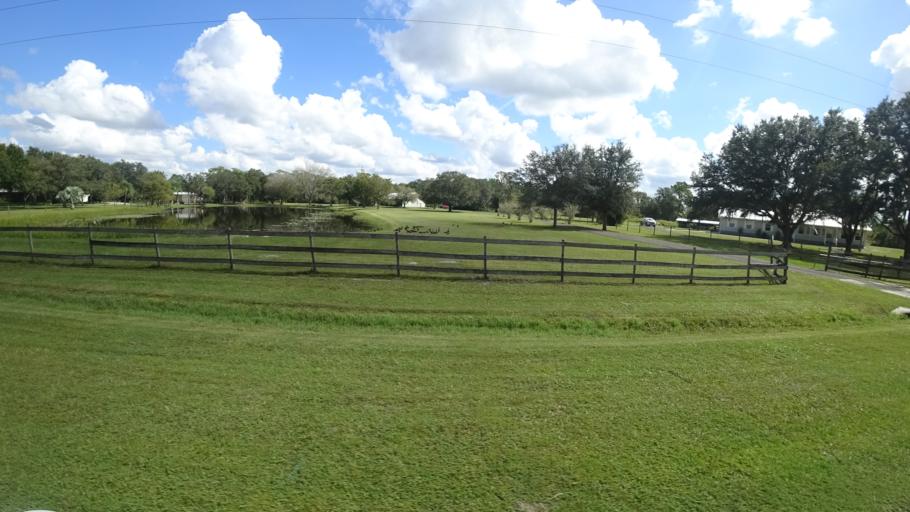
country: US
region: Florida
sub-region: Sarasota County
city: Lake Sarasota
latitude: 27.2820
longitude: -82.2237
